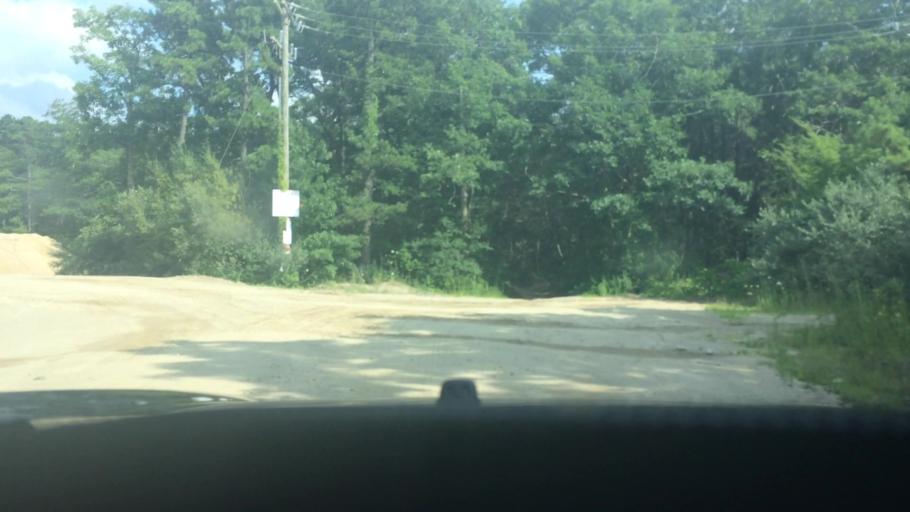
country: US
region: Massachusetts
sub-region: Barnstable County
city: Forestdale
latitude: 41.7231
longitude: -70.4846
